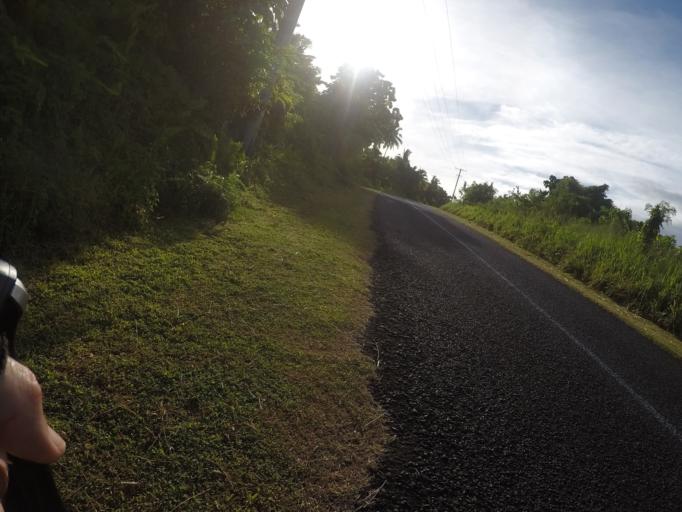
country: WS
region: Vaisigano
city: Asau
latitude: -13.6147
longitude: -172.6923
